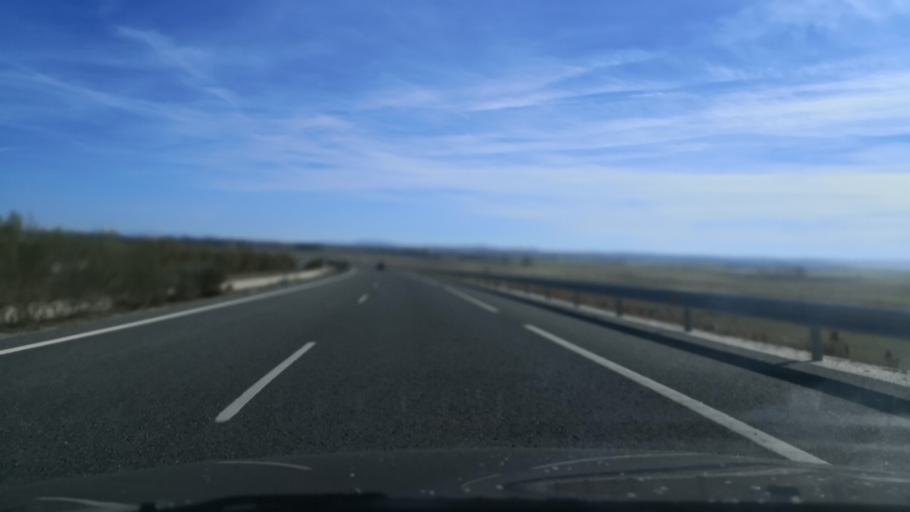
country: ES
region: Castille and Leon
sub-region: Provincia de Avila
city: Munogrande
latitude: 40.8163
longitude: -4.9213
